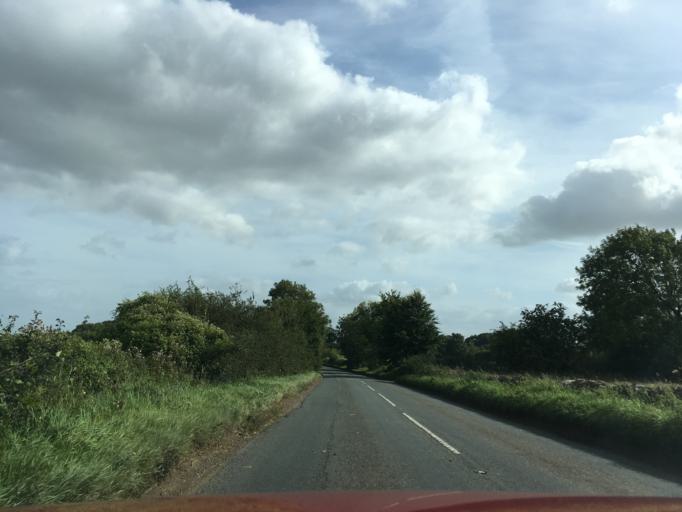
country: GB
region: England
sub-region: Gloucestershire
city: Stonehouse
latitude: 51.6934
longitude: -2.2832
